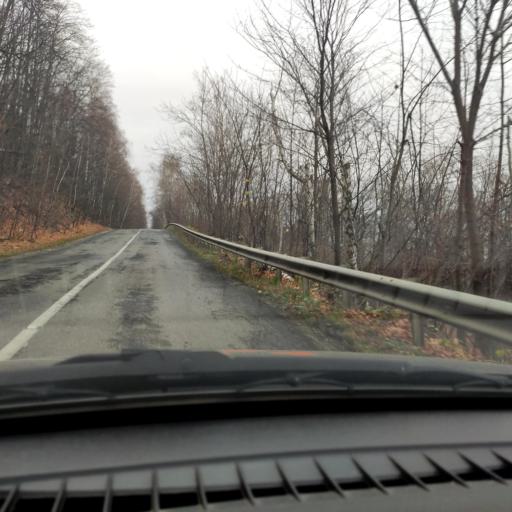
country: RU
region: Samara
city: Povolzhskiy
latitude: 53.4387
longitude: 49.6935
